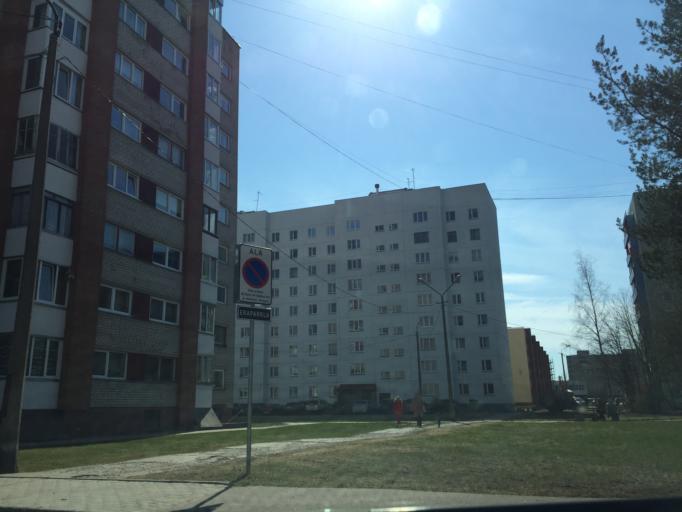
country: EE
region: Ida-Virumaa
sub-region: Narva linn
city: Narva
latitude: 59.3909
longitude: 28.1683
